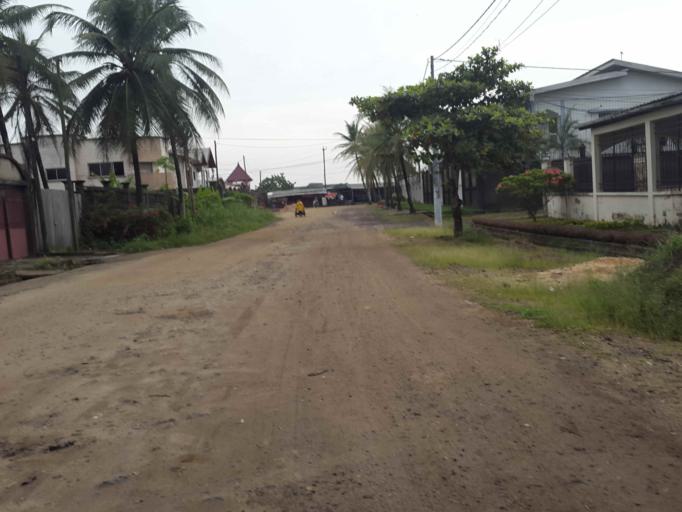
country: CM
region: Littoral
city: Douala
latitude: 4.0929
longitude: 9.7302
